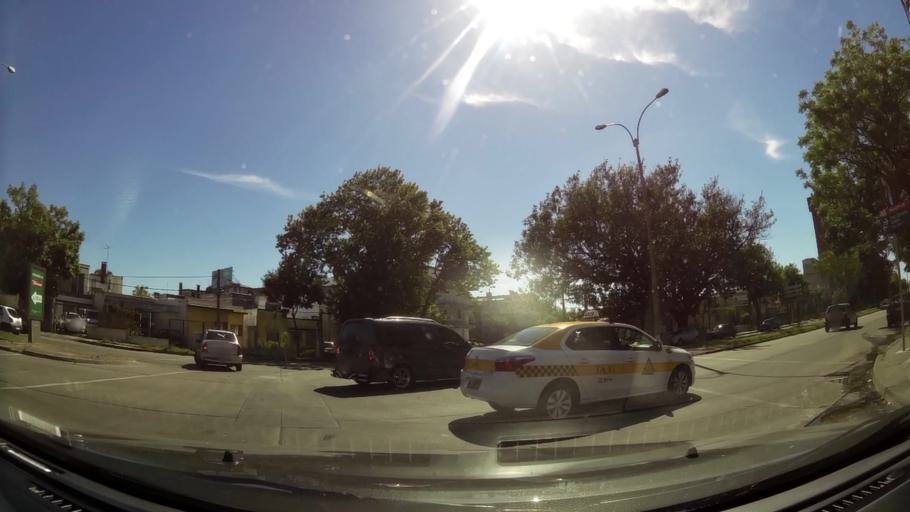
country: UY
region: Montevideo
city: Montevideo
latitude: -34.8878
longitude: -56.1366
